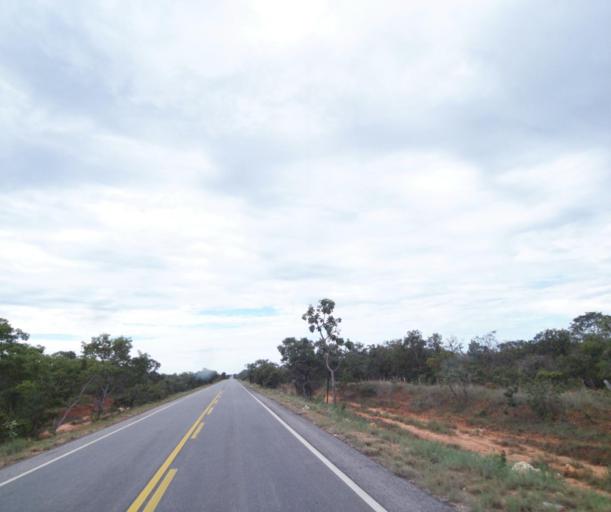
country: BR
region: Bahia
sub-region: Sao Felix Do Coribe
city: Santa Maria da Vitoria
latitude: -13.9691
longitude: -44.4461
